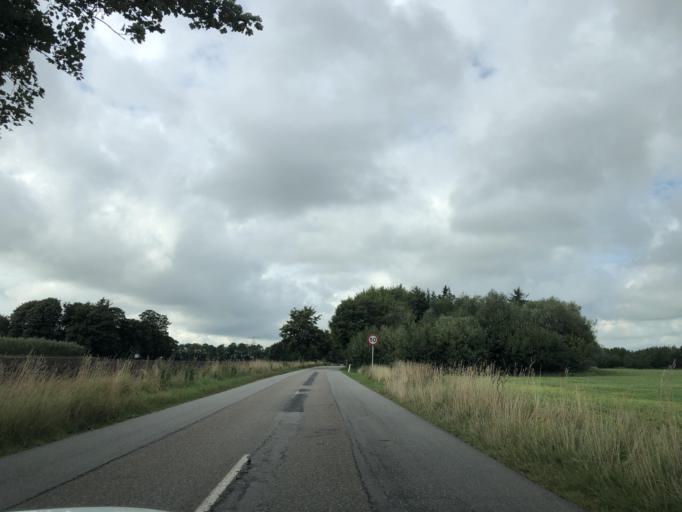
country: DK
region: North Denmark
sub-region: Alborg Kommune
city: Svenstrup
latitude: 56.9412
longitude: 9.7920
